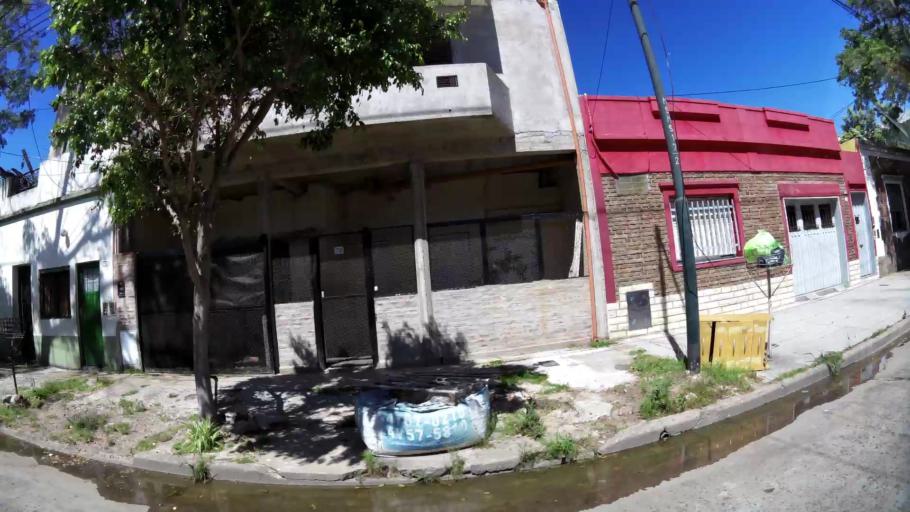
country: AR
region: Buenos Aires
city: Caseros
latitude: -34.5902
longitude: -58.5491
